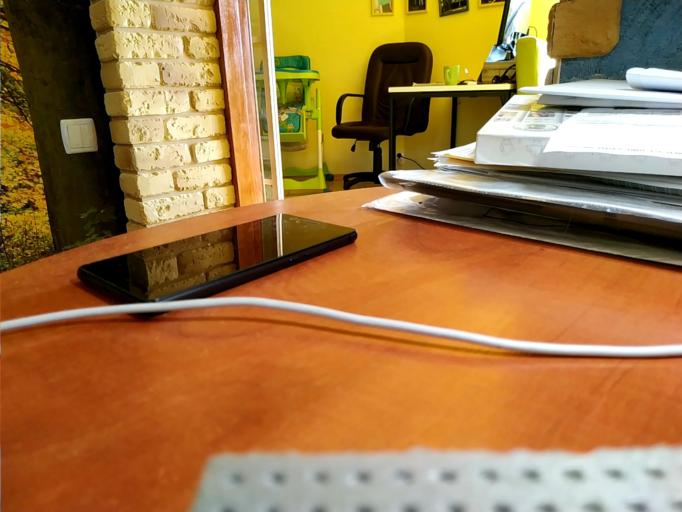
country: RU
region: Tverskaya
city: Kalashnikovo
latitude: 57.3661
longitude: 35.4414
